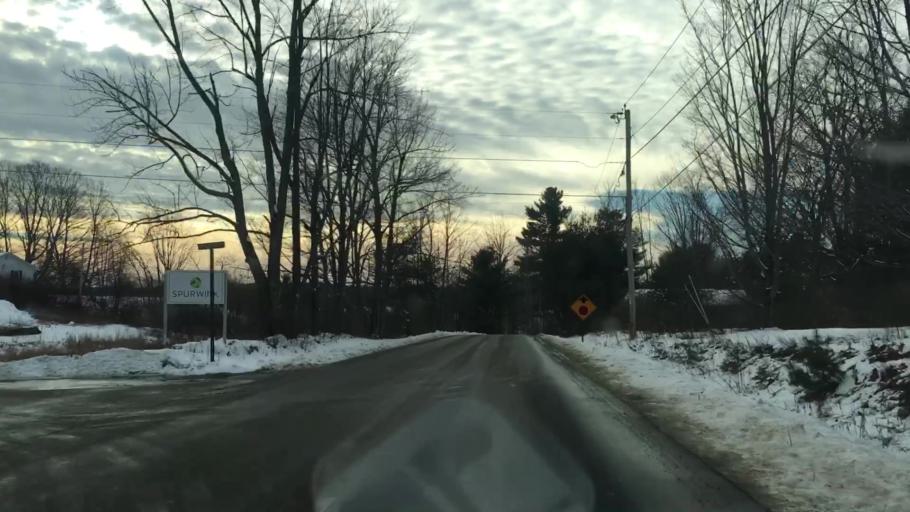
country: US
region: Maine
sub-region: Kennebec County
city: Farmingdale
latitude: 44.2585
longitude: -69.7611
